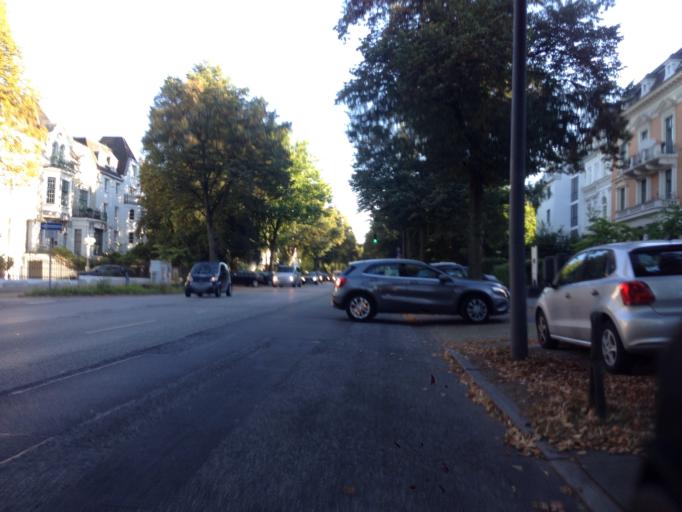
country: DE
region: Hamburg
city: Hamburg-Nord
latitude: 53.5797
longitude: 9.9888
